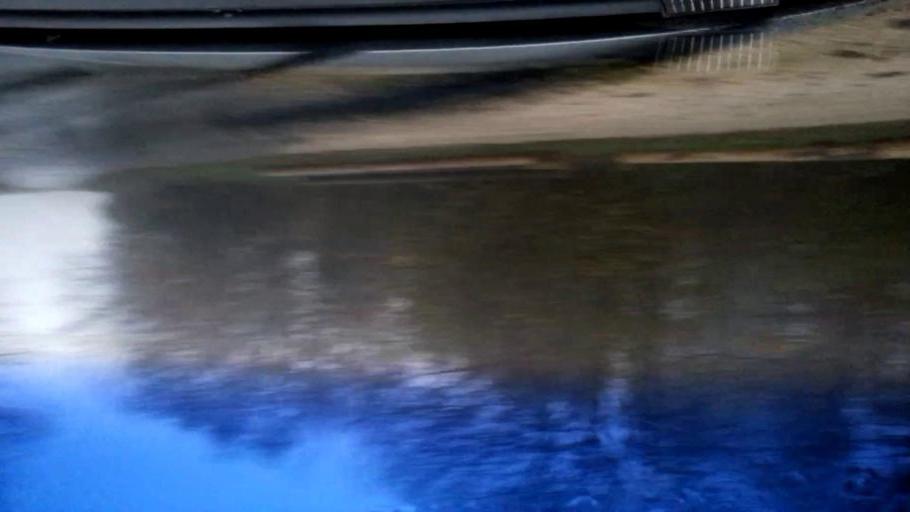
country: DE
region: Bavaria
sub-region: Upper Franconia
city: Poxdorf
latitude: 49.9335
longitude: 11.0681
